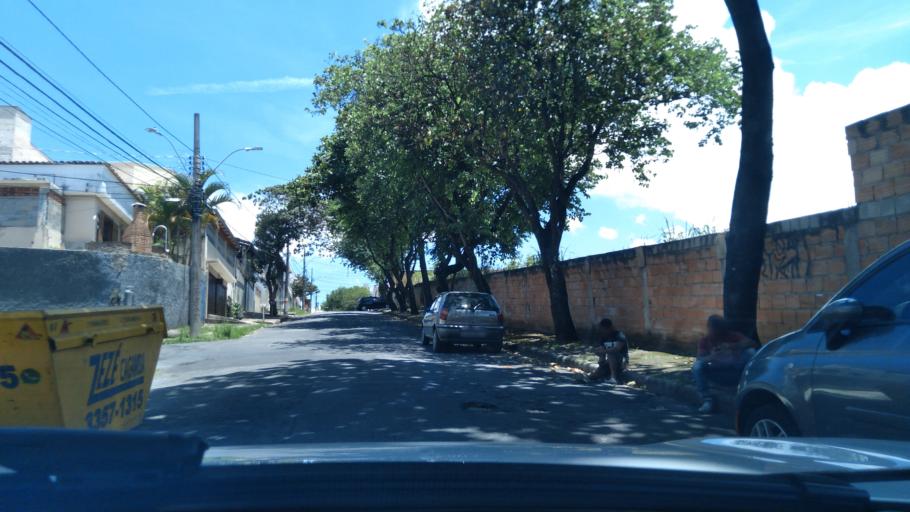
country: BR
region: Minas Gerais
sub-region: Contagem
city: Contagem
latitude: -19.9251
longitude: -43.9969
